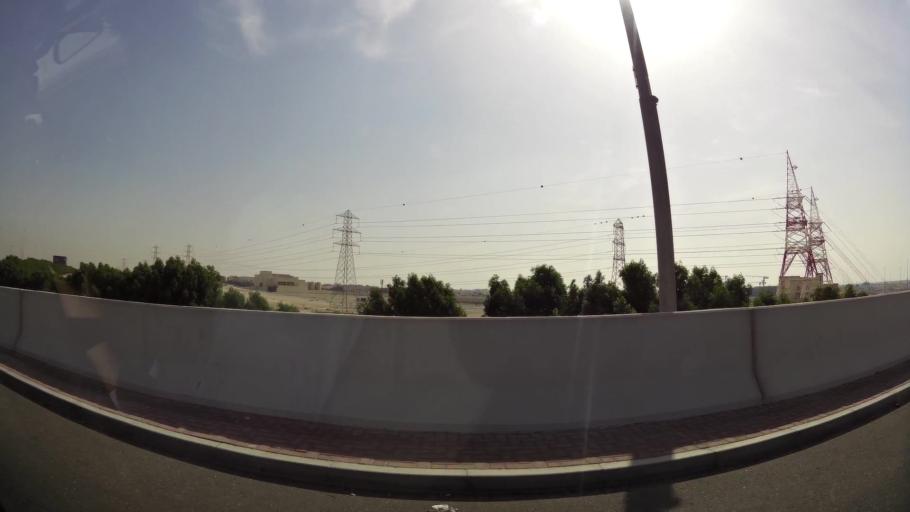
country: AE
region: Ash Shariqah
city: Sharjah
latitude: 25.2365
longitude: 55.4048
